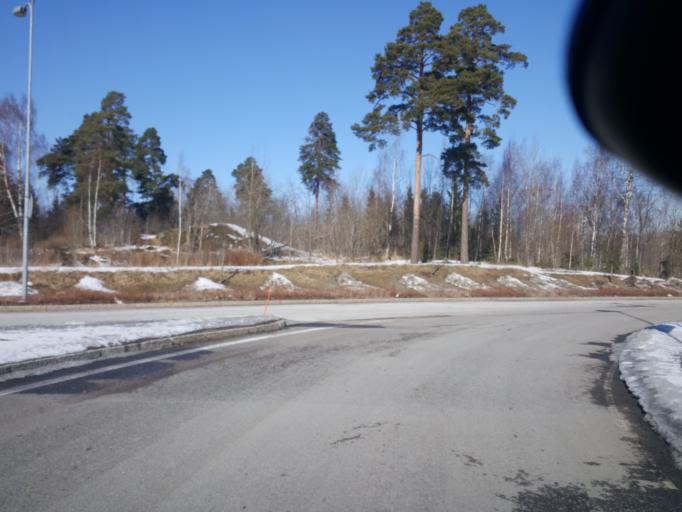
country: FI
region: Uusimaa
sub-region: Helsinki
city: Teekkarikylae
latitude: 60.2091
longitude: 24.8317
